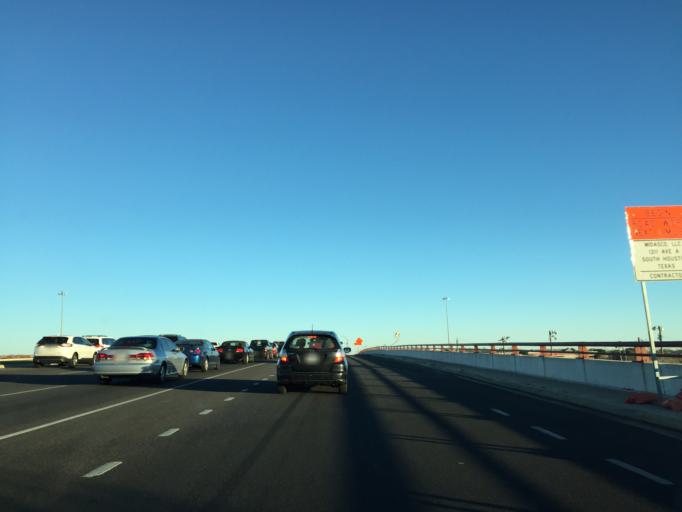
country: US
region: Texas
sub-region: Travis County
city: Wells Branch
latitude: 30.4217
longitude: -97.7071
